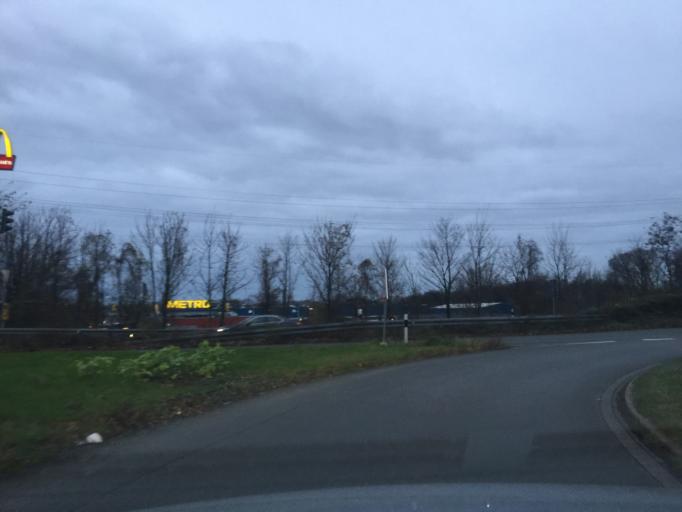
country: DE
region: North Rhine-Westphalia
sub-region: Regierungsbezirk Dusseldorf
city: Oberhausen
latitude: 51.4591
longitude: 6.8861
